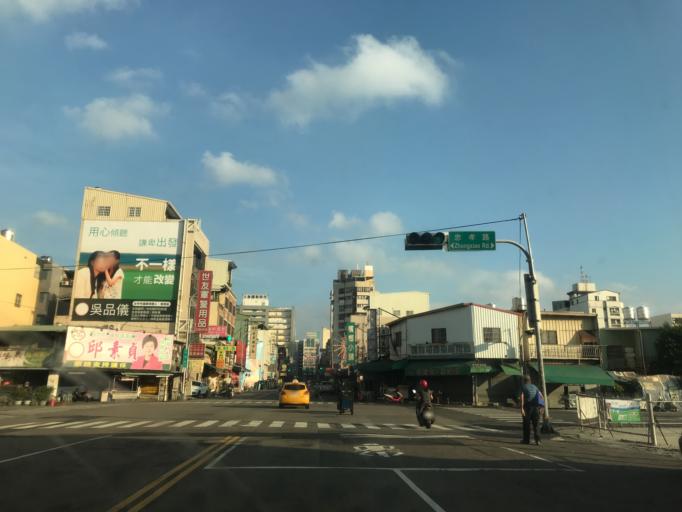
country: TW
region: Taiwan
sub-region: Taichung City
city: Taichung
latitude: 24.1324
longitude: 120.6899
